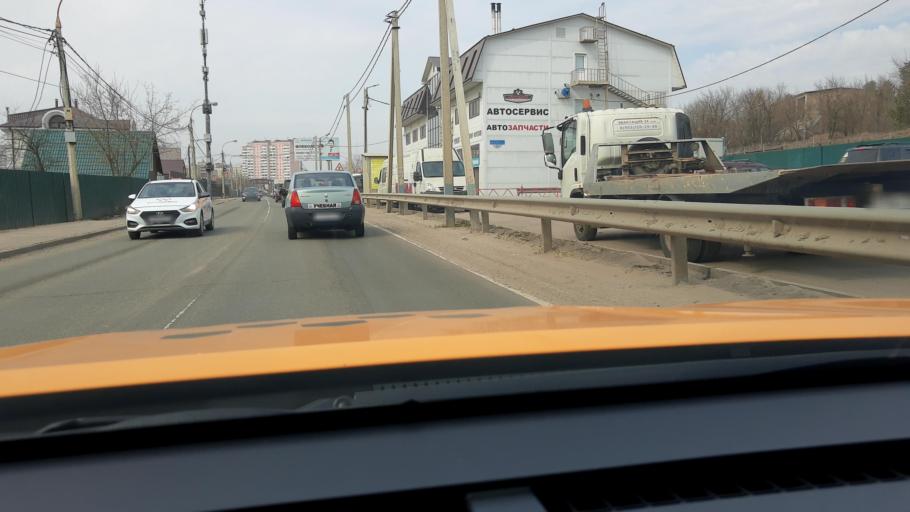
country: RU
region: Moskovskaya
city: Zhukovskiy
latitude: 55.5896
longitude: 38.1022
